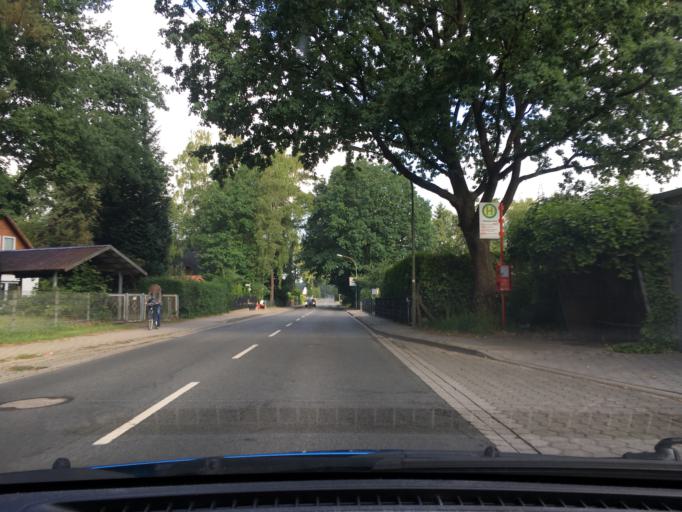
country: DE
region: Lower Saxony
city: Buchholz in der Nordheide
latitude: 53.3267
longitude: 9.8413
